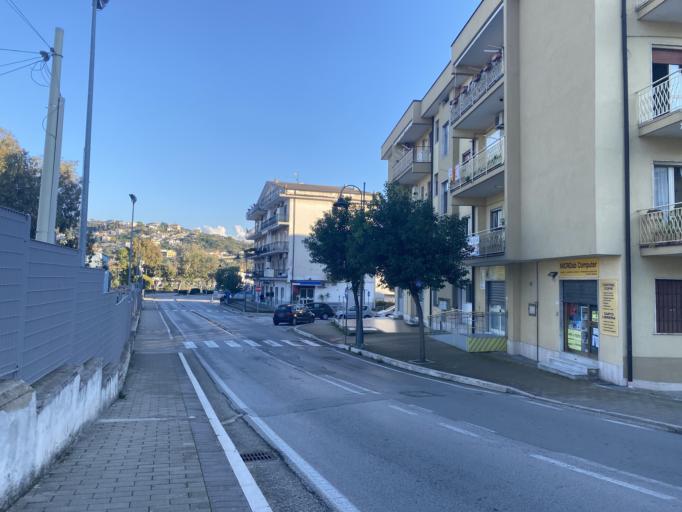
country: IT
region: Campania
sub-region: Provincia di Salerno
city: Agropoli
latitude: 40.3497
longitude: 14.9928
